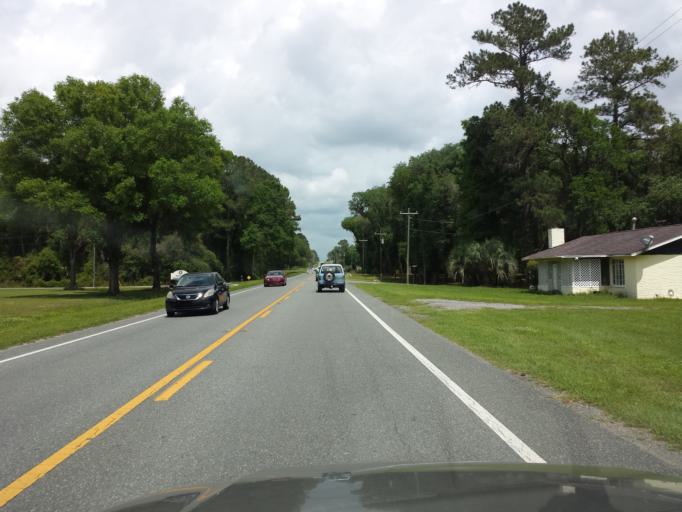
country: US
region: Florida
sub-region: Columbia County
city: Watertown
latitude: 30.0394
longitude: -82.5979
